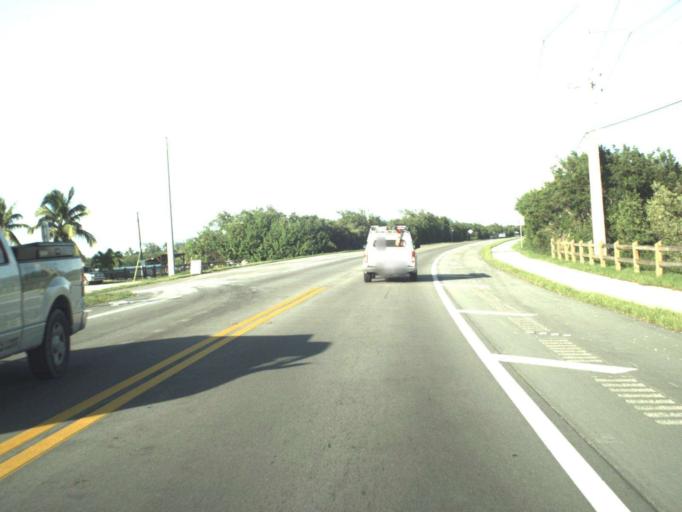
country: US
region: Florida
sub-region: Monroe County
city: Islamorada
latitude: 24.8372
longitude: -80.7989
